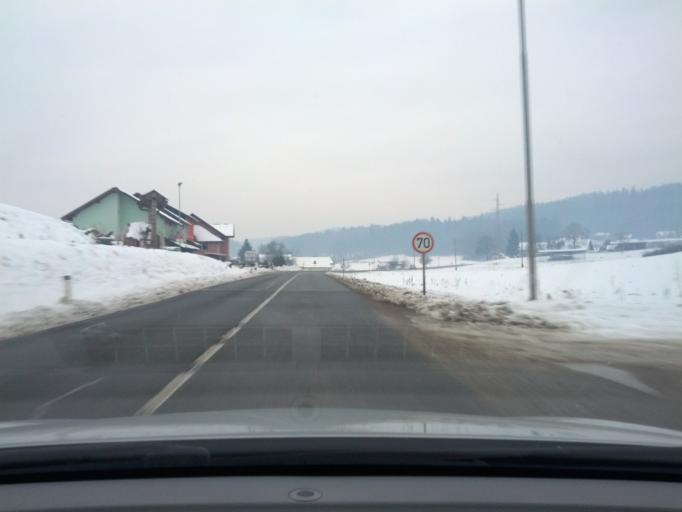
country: SI
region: Moravce
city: Moravce
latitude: 46.1378
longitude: 14.7171
